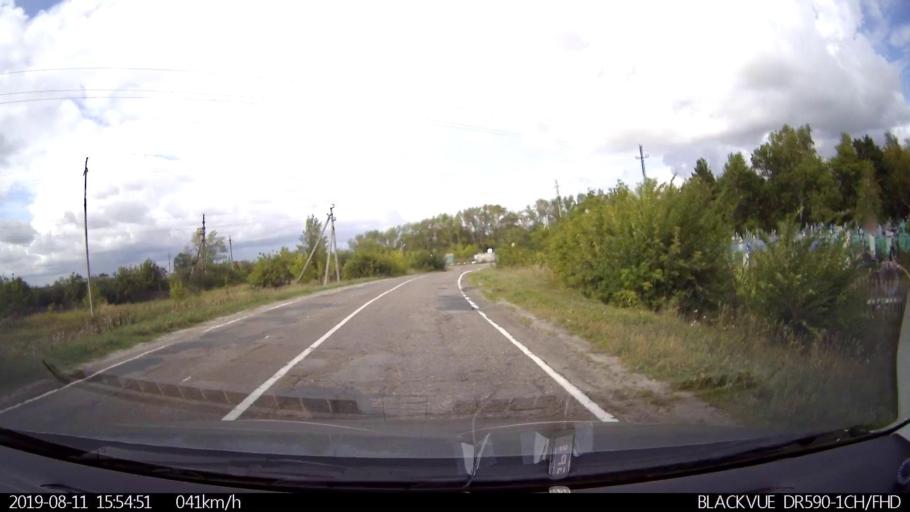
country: RU
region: Ulyanovsk
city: Ignatovka
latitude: 53.9434
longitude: 47.6560
